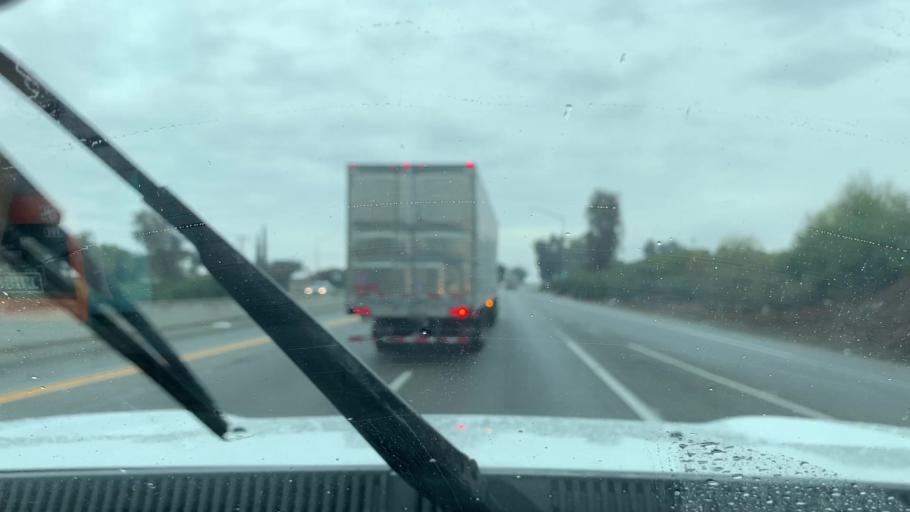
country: US
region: California
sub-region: Kern County
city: Delano
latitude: 35.7774
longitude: -119.2527
